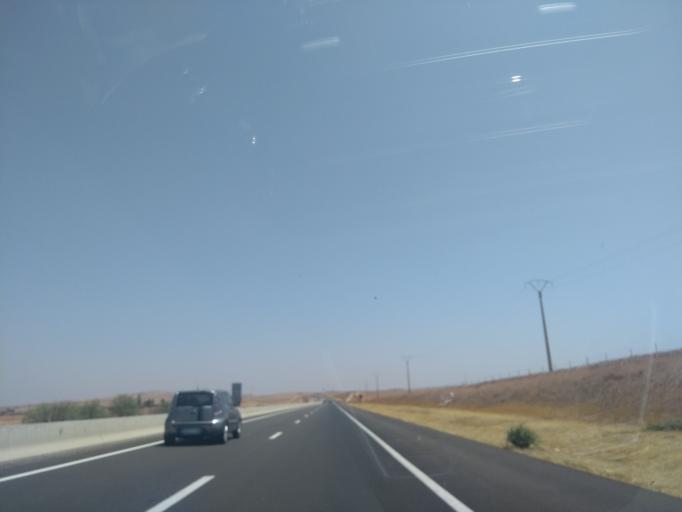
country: MA
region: Marrakech-Tensift-Al Haouz
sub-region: Kelaa-Des-Sraghna
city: Sidi Abdallah
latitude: 32.2877
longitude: -7.9643
